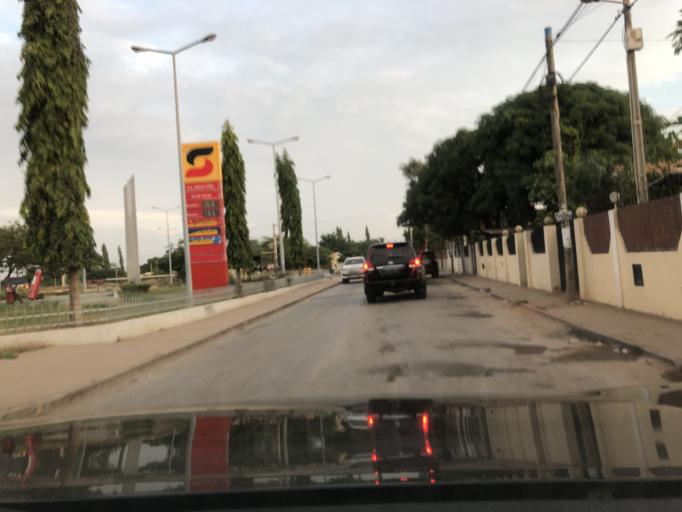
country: AO
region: Luanda
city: Luanda
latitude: -8.8973
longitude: 13.2286
